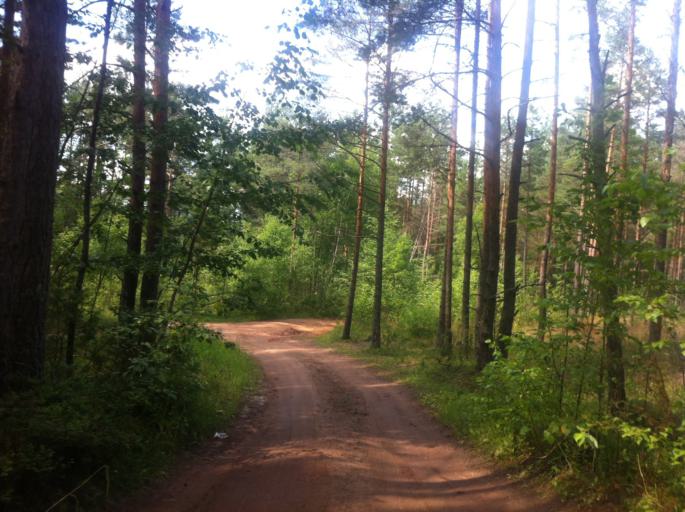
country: RU
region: Pskov
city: Izborsk
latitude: 57.8333
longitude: 27.9371
